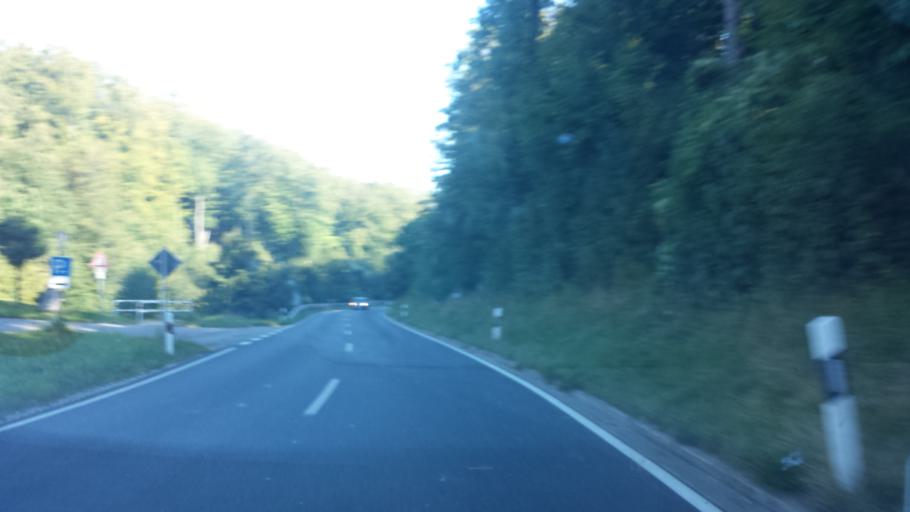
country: DE
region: Bavaria
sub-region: Lower Bavaria
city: Ihrlerstein
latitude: 48.9108
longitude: 11.8633
